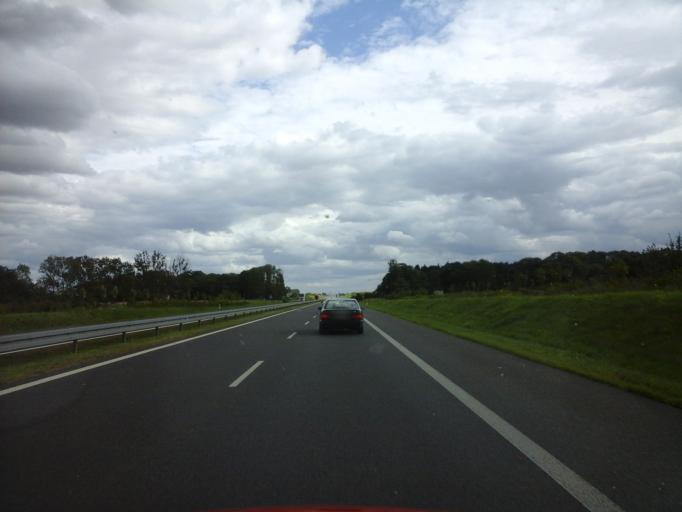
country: PL
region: West Pomeranian Voivodeship
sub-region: Powiat pyrzycki
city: Warnice
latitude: 53.3125
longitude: 14.9909
